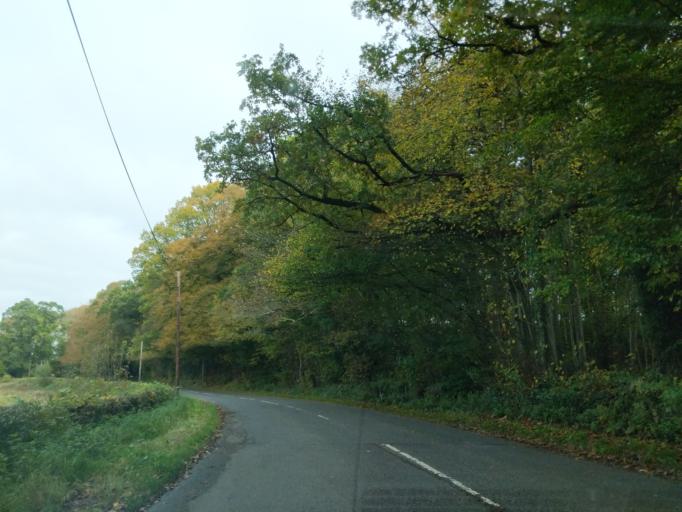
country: GB
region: Scotland
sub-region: Dumfries and Galloway
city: Thornhill
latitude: 55.2405
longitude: -3.7755
